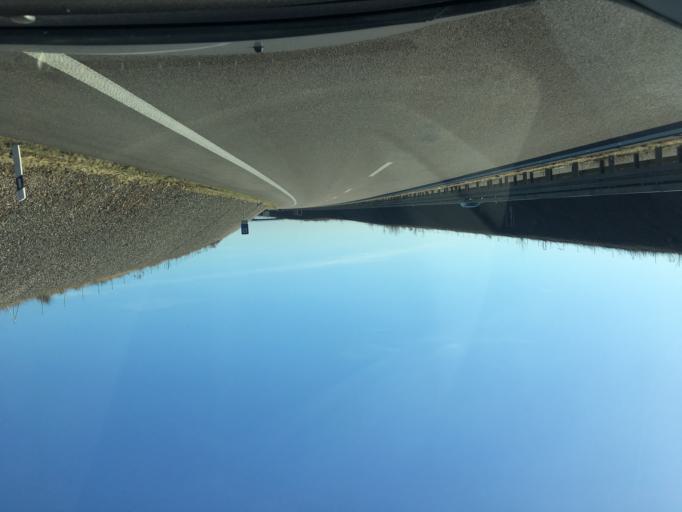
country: DE
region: Saxony
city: Geithain
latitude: 51.0308
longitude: 12.6866
